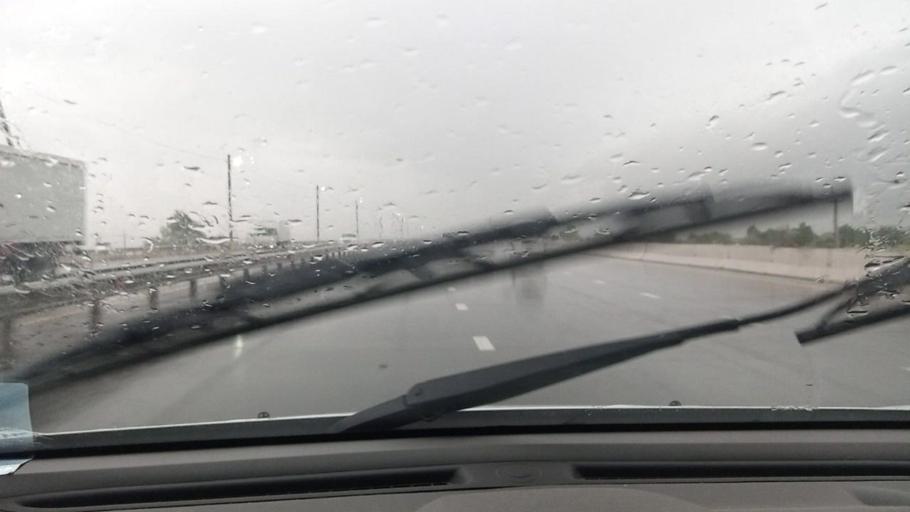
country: UZ
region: Toshkent
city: Ohangaron
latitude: 40.9273
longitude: 69.5964
